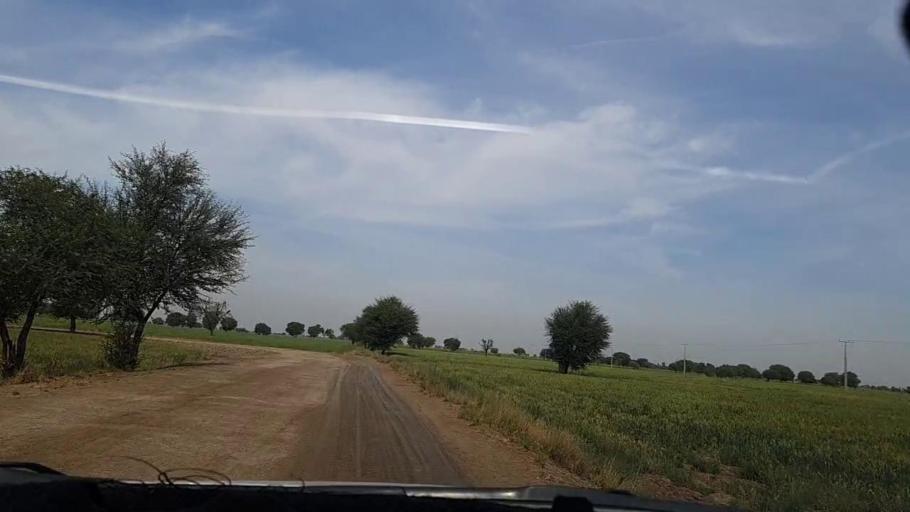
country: PK
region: Sindh
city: Dhoro Naro
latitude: 25.4496
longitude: 69.4974
